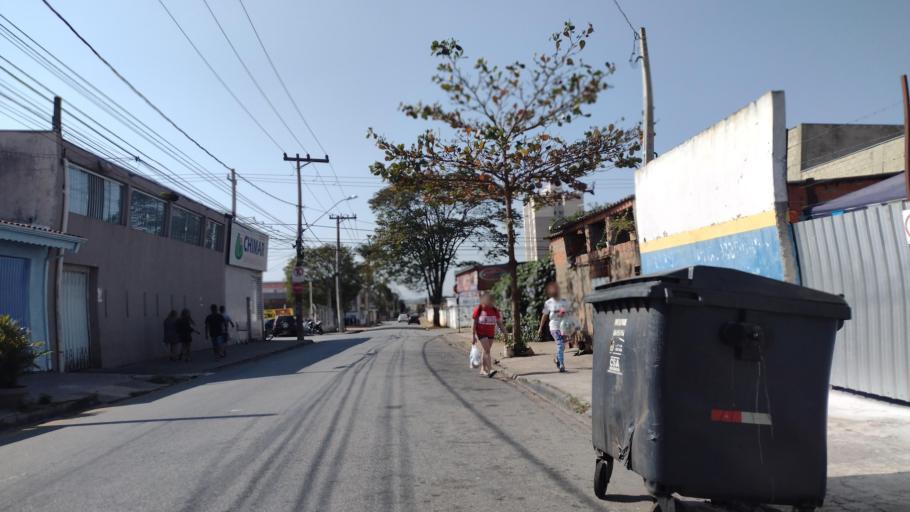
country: BR
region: Sao Paulo
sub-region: Sorocaba
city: Sorocaba
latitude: -23.4221
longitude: -47.4148
